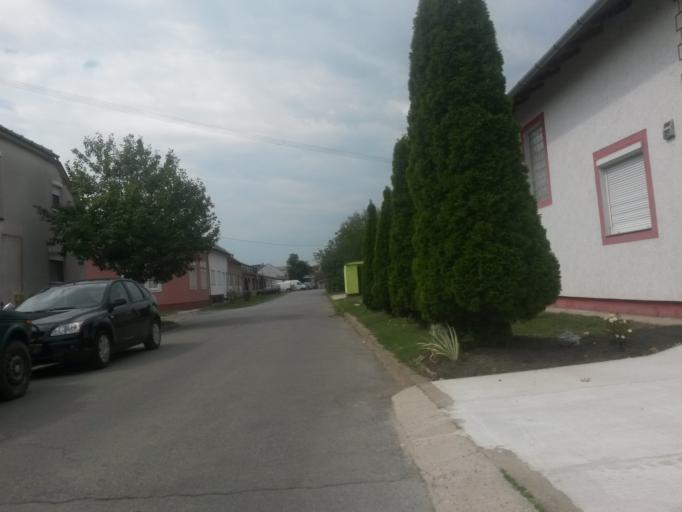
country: HR
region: Osjecko-Baranjska
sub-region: Grad Osijek
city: Osijek
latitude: 45.5520
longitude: 18.6809
